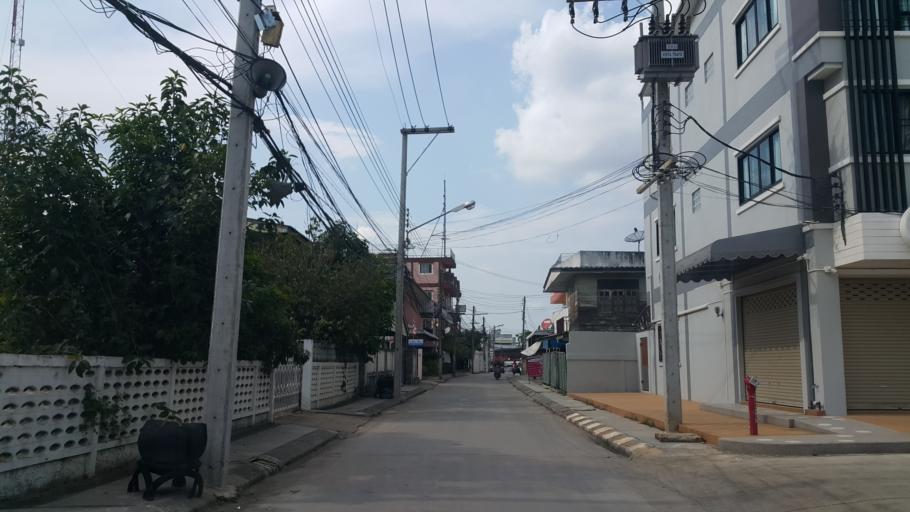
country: TH
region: Chiang Rai
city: Chiang Rai
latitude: 19.9018
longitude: 99.8314
